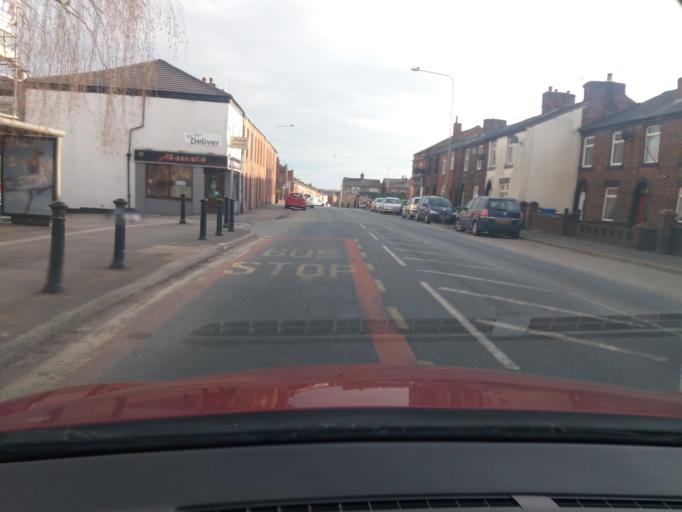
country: GB
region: England
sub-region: Lancashire
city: Chorley
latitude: 53.6508
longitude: -2.6174
